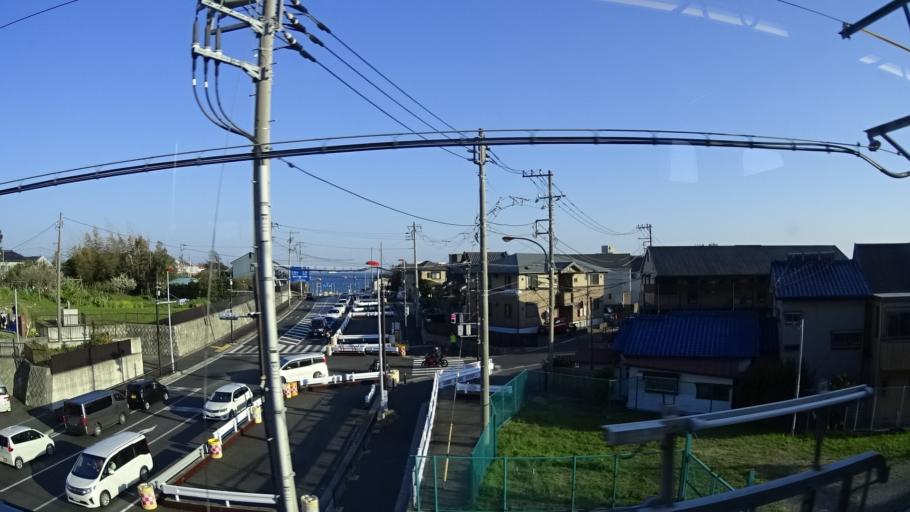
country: JP
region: Kanagawa
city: Yokosuka
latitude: 35.2070
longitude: 139.6779
